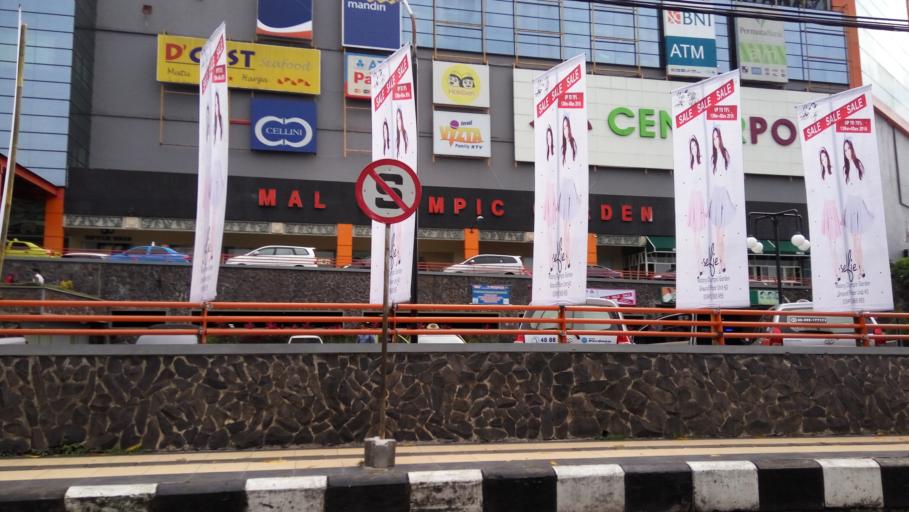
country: ID
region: East Java
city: Malang
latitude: -7.9777
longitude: 112.6235
